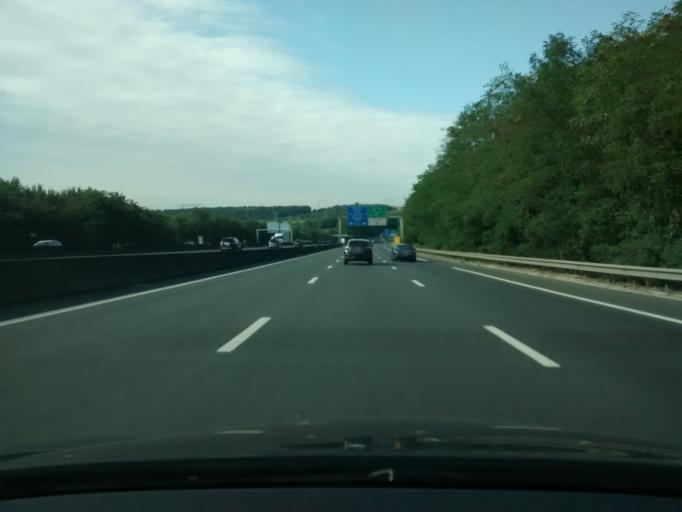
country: FR
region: Ile-de-France
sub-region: Departement de l'Essonne
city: Les Ulis
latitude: 48.6657
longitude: 2.1901
